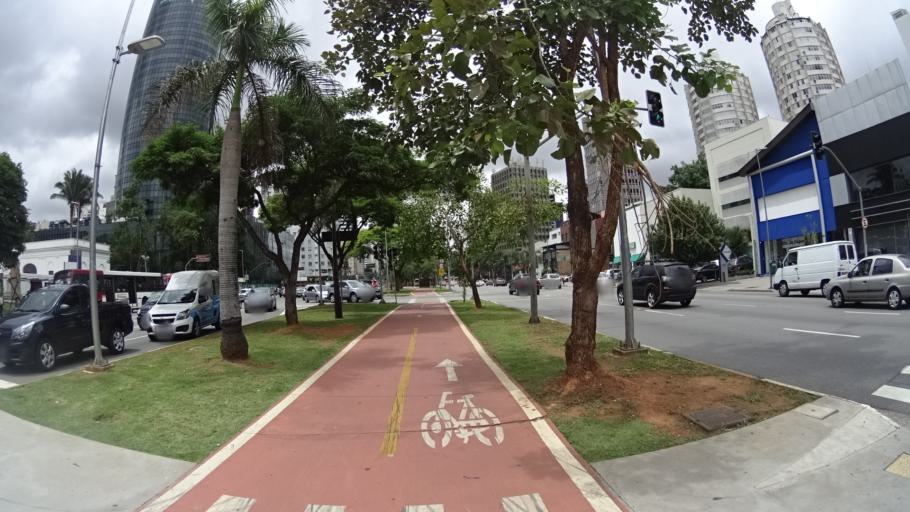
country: BR
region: Sao Paulo
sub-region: Sao Paulo
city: Sao Paulo
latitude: -23.5800
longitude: -46.6853
